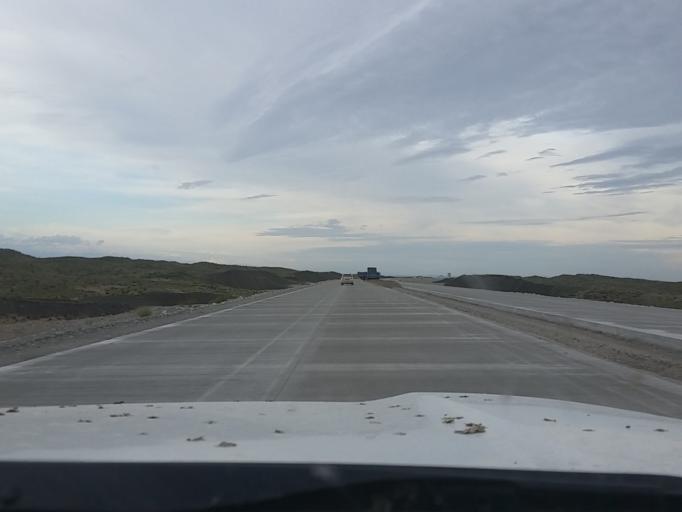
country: KZ
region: Almaty Oblysy
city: Zharkent
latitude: 44.1742
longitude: 80.3291
